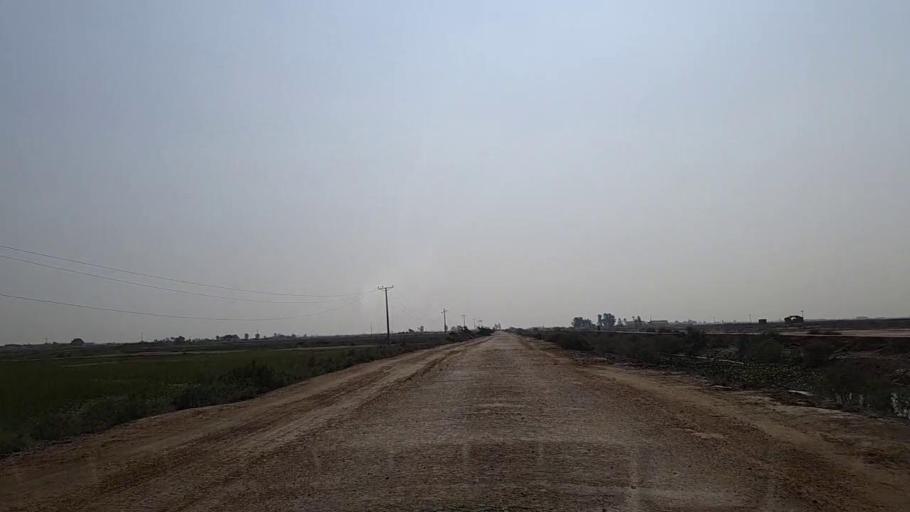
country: PK
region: Sindh
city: Thatta
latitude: 24.7160
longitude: 67.7684
